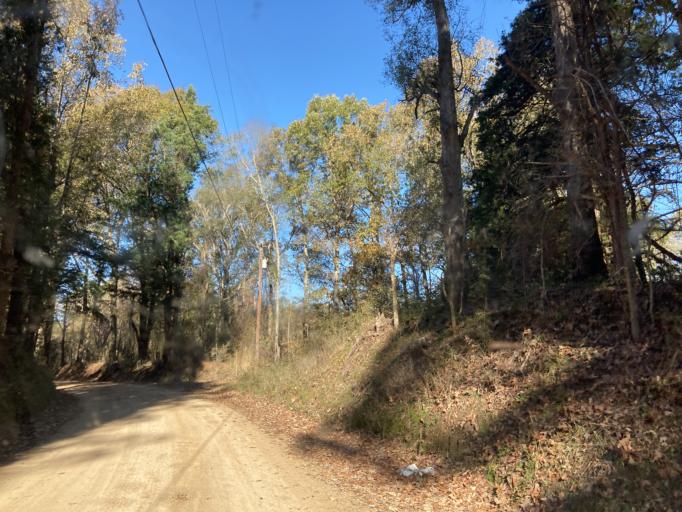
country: US
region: Mississippi
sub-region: Yazoo County
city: Yazoo City
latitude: 32.6985
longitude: -90.4948
